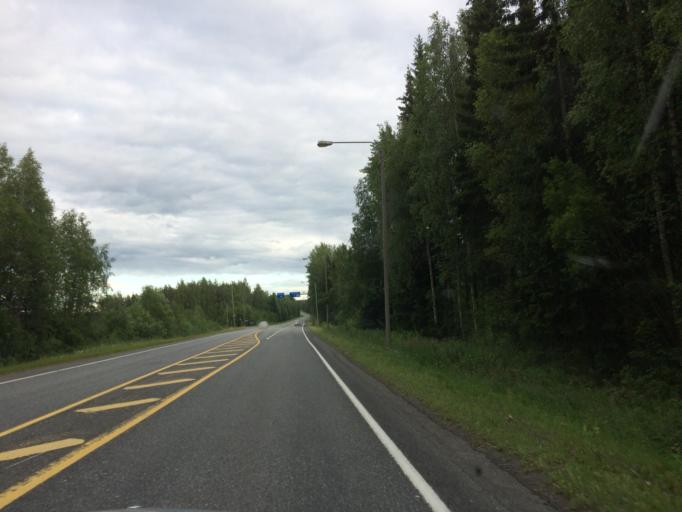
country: FI
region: Haeme
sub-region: Haemeenlinna
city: Haemeenlinna
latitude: 60.9430
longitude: 24.5176
